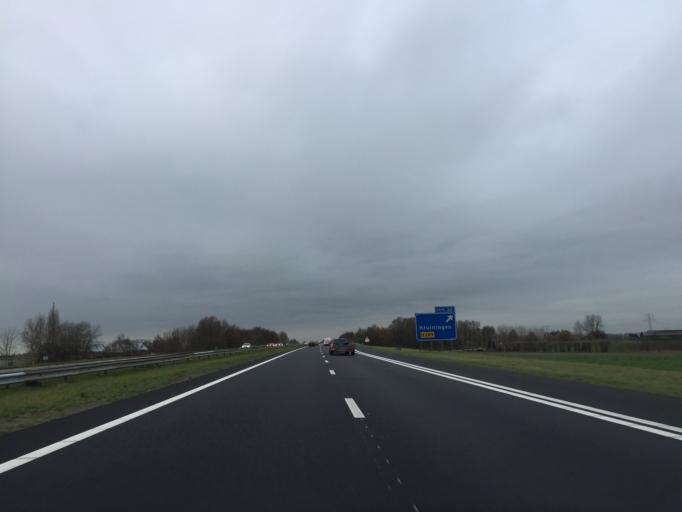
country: NL
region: Zeeland
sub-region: Gemeente Reimerswaal
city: Yerseke
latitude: 51.4330
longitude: 4.0736
